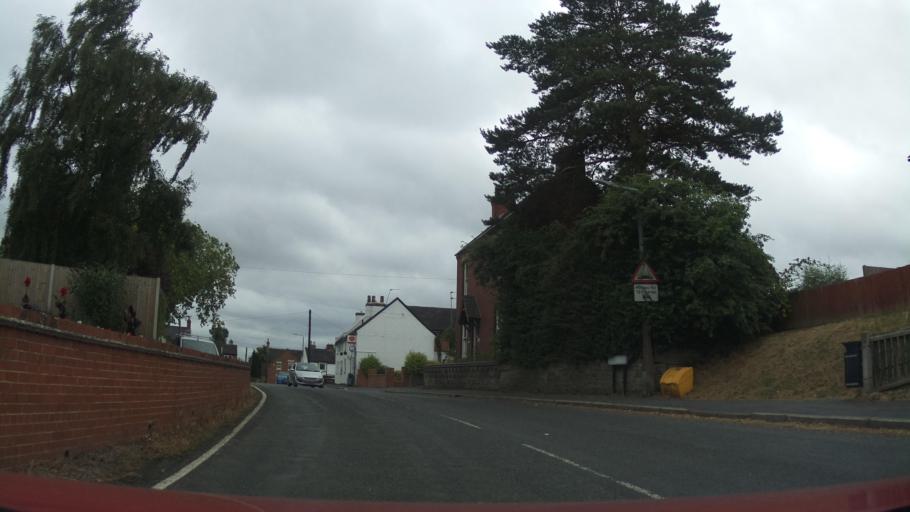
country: GB
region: England
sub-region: Derbyshire
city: Findern
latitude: 52.8713
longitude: -1.5441
